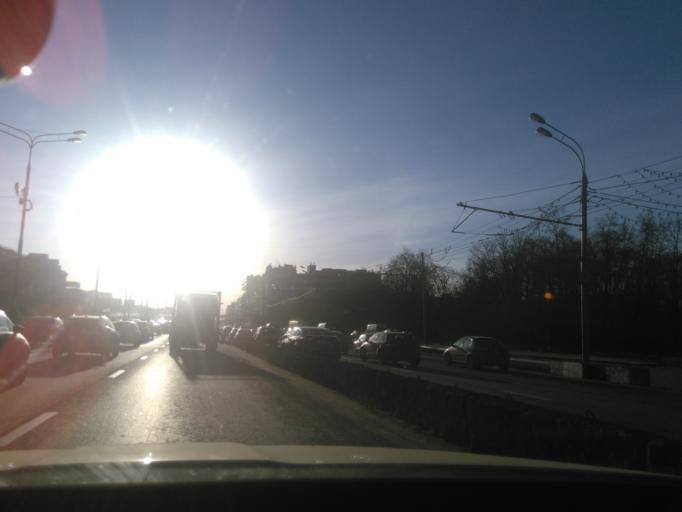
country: RU
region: Moscow
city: Sokol
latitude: 55.8033
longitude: 37.5203
